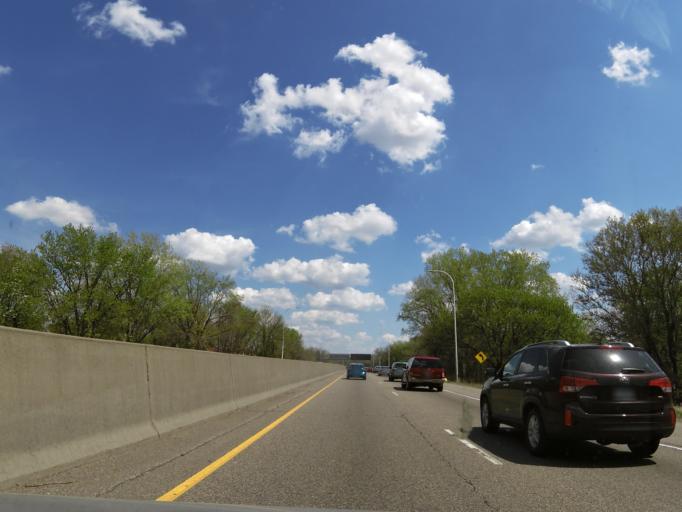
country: US
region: Minnesota
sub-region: Hennepin County
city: Richfield
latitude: 44.8906
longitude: -93.2628
